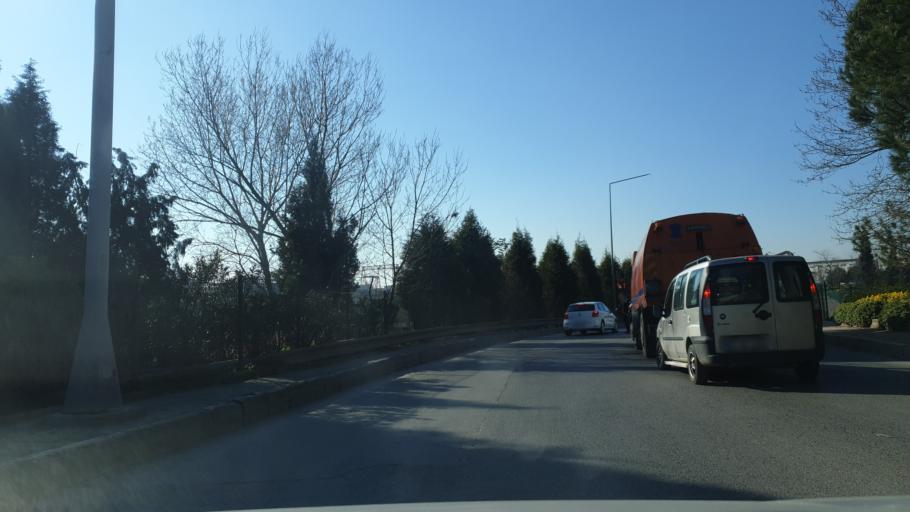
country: TR
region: Istanbul
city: Icmeler
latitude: 40.8788
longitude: 29.3592
